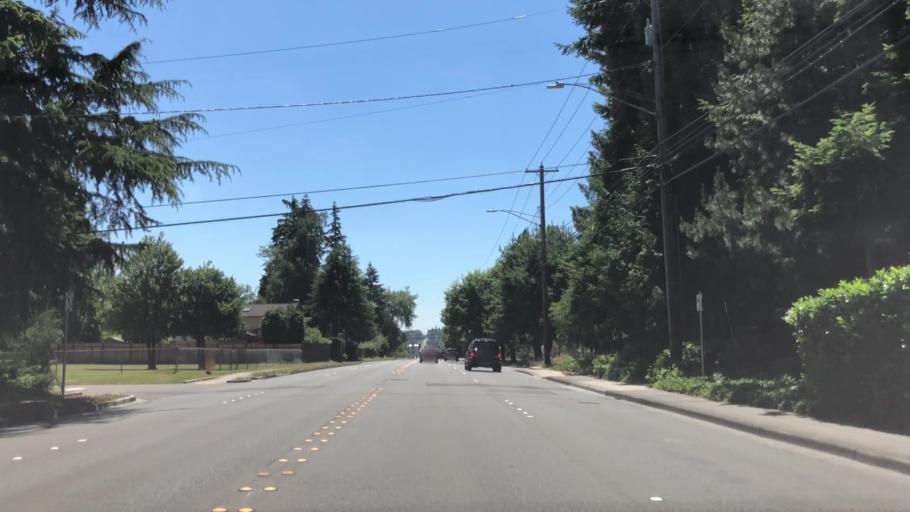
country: US
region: Washington
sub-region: Snohomish County
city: Alderwood Manor
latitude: 47.8260
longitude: -122.2925
